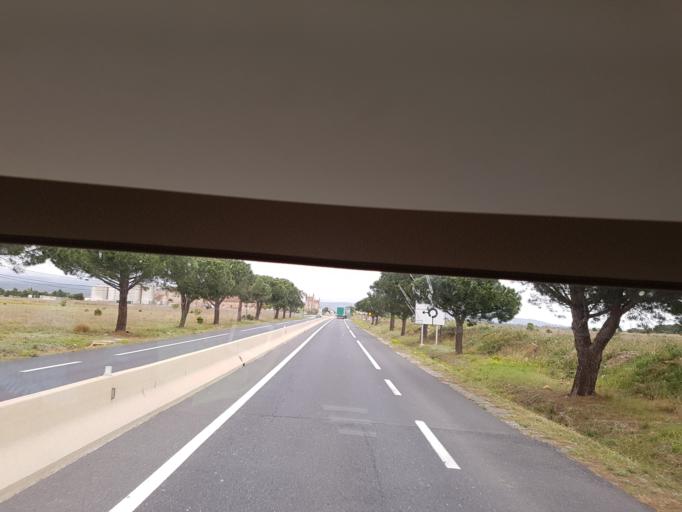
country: FR
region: Languedoc-Roussillon
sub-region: Departement des Pyrenees-Orientales
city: Rivesaltes
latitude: 42.7888
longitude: 2.9064
